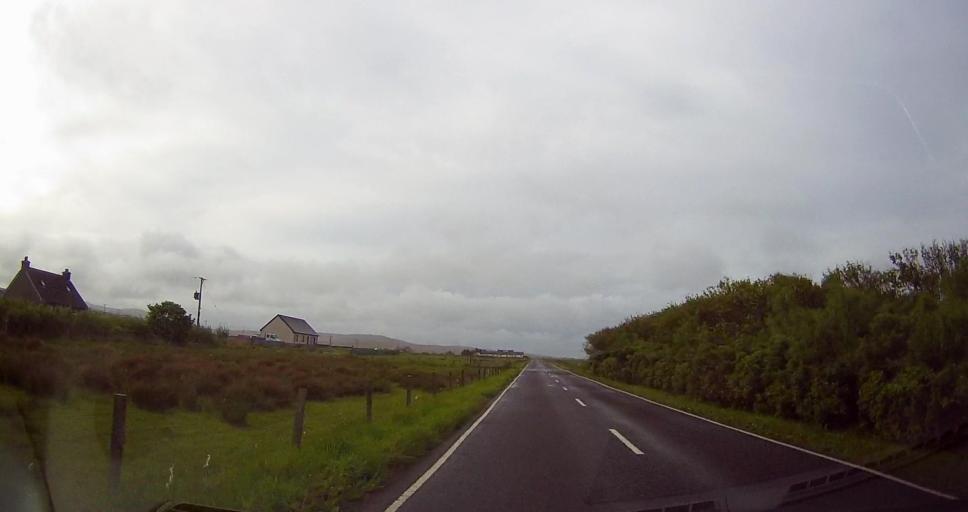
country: GB
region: Scotland
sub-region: Orkney Islands
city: Stromness
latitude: 58.9774
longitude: -3.2421
